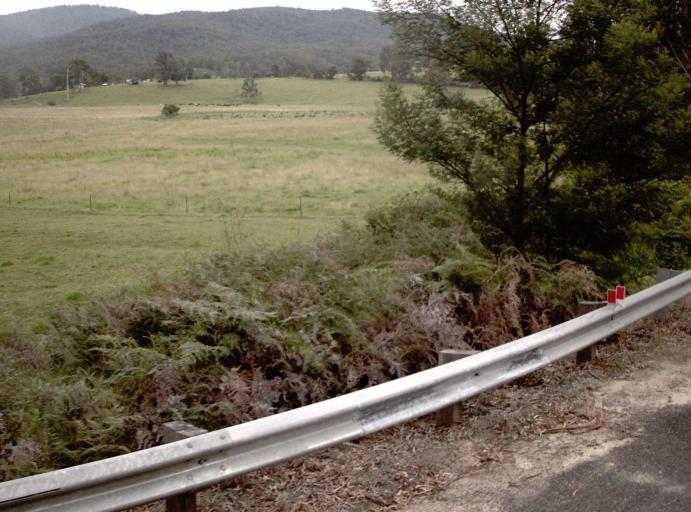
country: AU
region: New South Wales
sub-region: Bombala
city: Bombala
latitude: -37.4812
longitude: 149.1809
